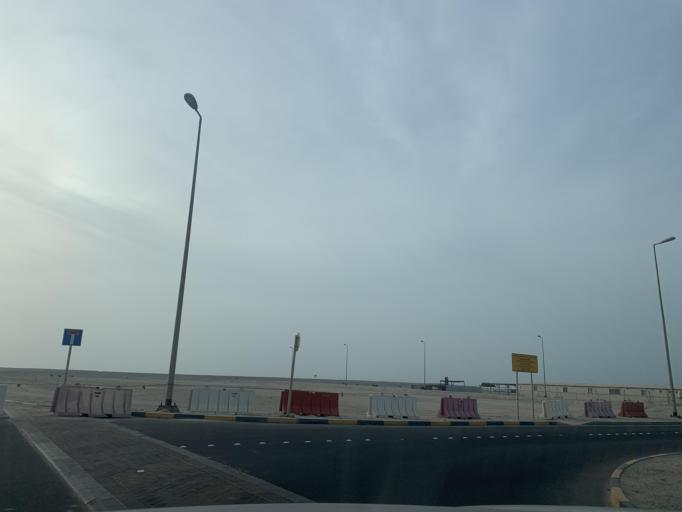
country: BH
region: Muharraq
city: Al Muharraq
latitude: 26.3088
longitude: 50.6174
